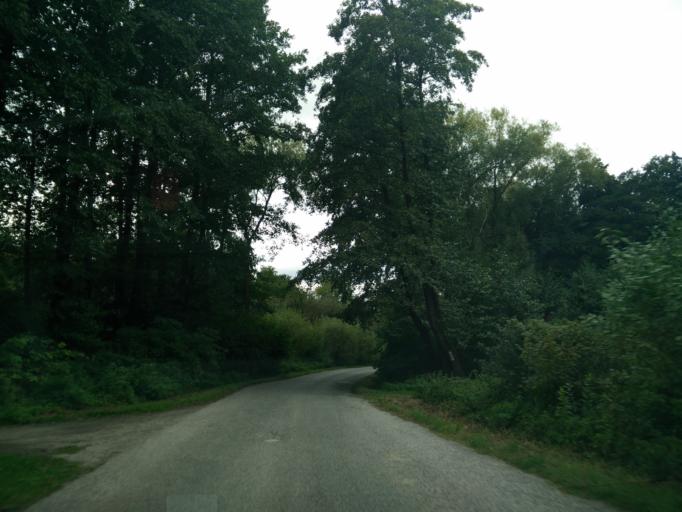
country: SK
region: Nitriansky
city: Novaky
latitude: 48.6256
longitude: 18.4919
